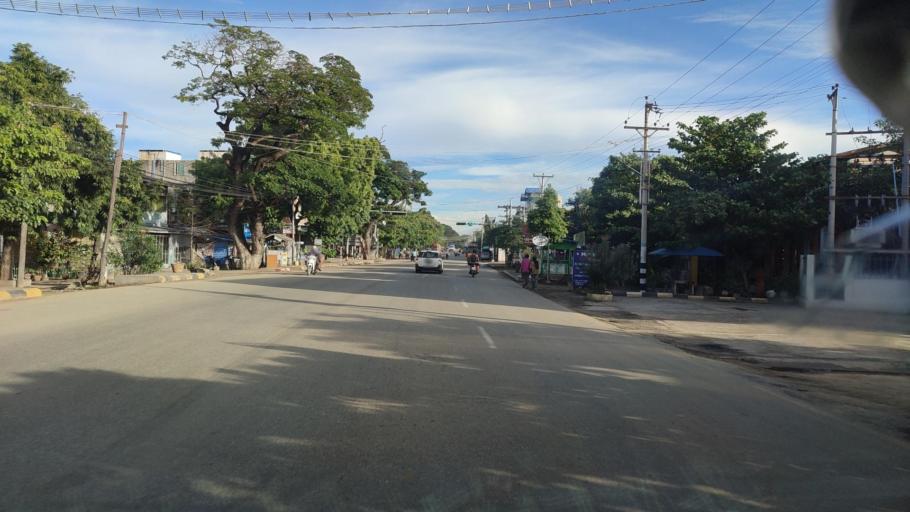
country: MM
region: Mandalay
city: Yamethin
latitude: 20.1342
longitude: 96.2000
